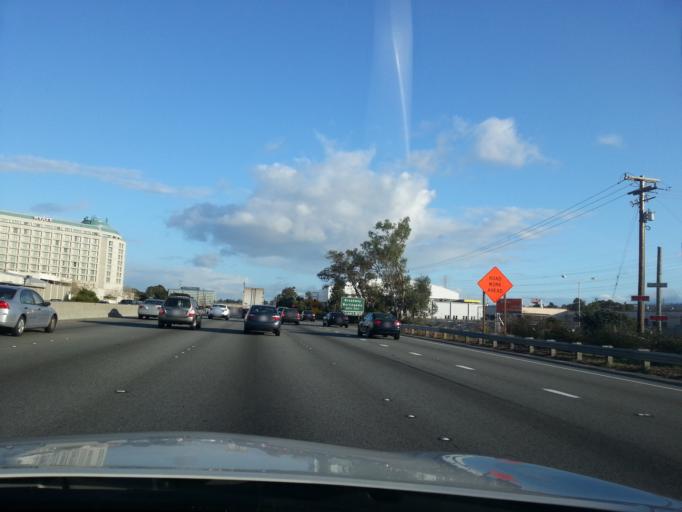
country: US
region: California
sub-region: San Mateo County
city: Burlingame
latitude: 37.5947
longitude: -122.3685
